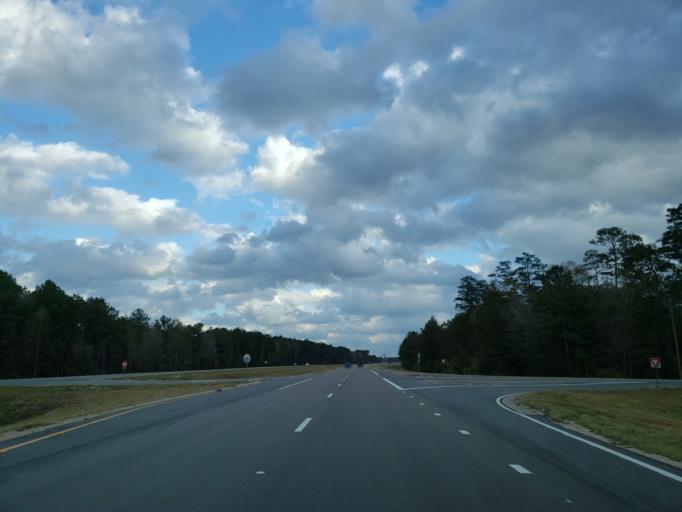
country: US
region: Mississippi
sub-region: Perry County
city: New Augusta
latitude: 31.2109
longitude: -89.1232
